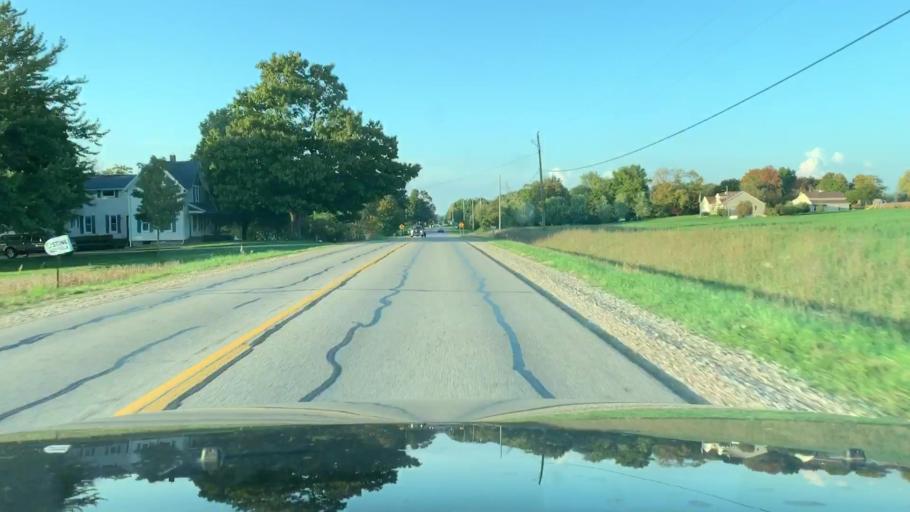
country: US
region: Michigan
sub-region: Ottawa County
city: Hudsonville
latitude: 42.8075
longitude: -85.8420
